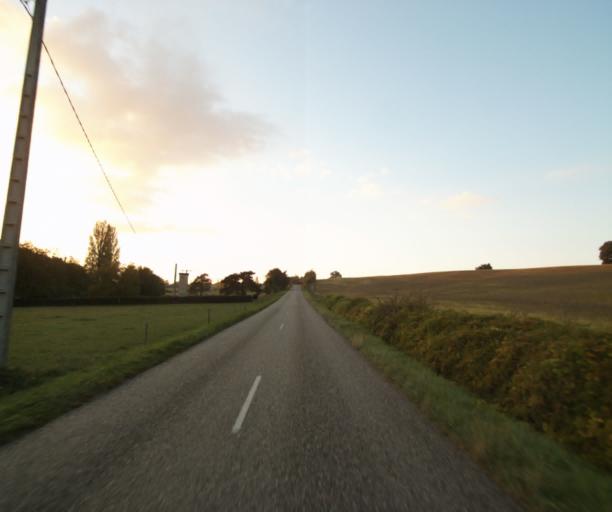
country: FR
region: Midi-Pyrenees
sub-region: Departement du Gers
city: Vic-Fezensac
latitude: 43.7926
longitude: 0.2518
